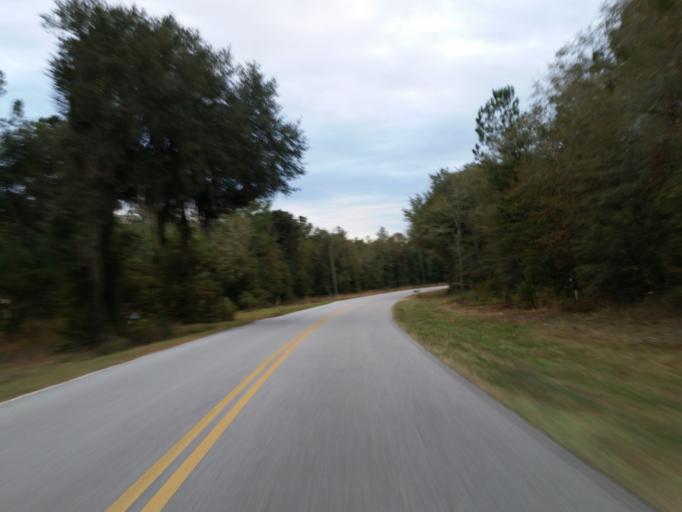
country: US
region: Florida
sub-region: Hamilton County
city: Jasper
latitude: 30.5539
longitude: -83.0996
